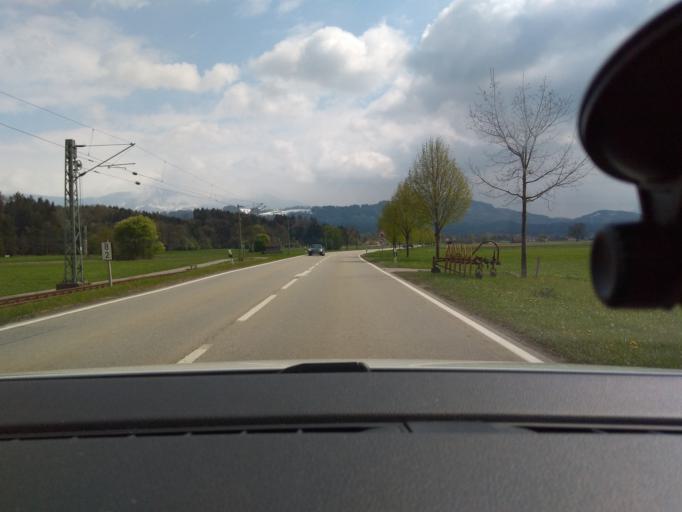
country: DE
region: Bavaria
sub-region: Upper Bavaria
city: Rohrdorf
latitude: 47.8140
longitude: 12.1599
